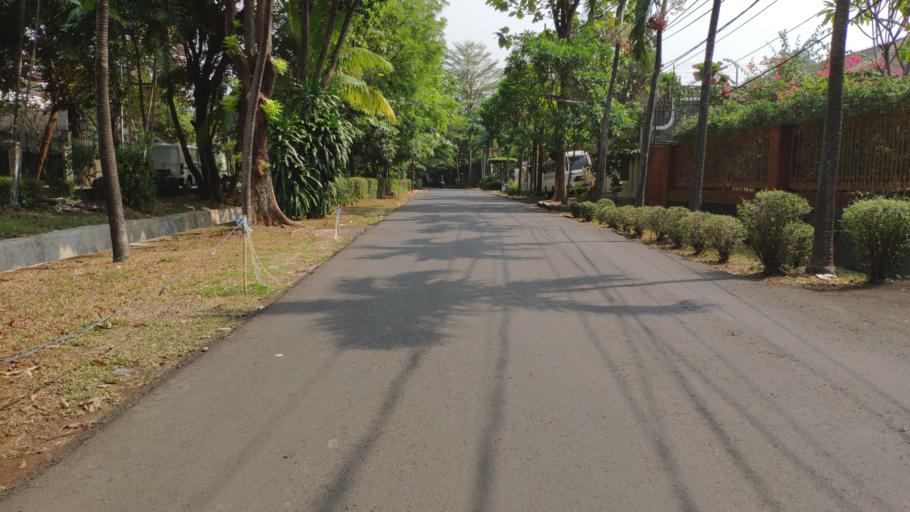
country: ID
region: Jakarta Raya
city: Jakarta
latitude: -6.2698
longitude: 106.8181
